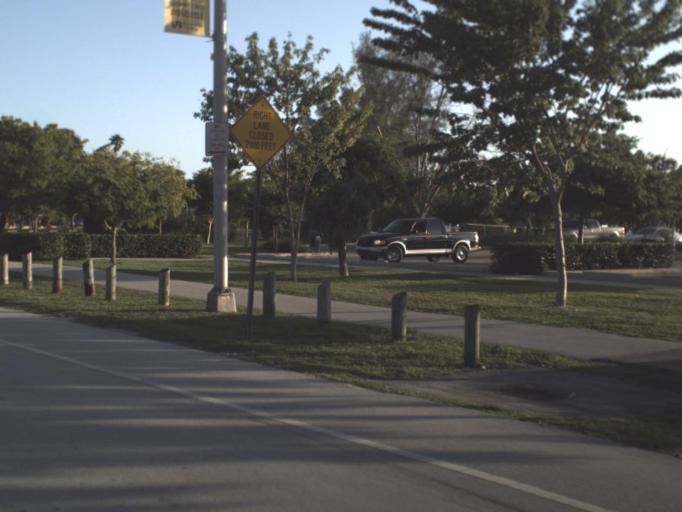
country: US
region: Florida
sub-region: Miami-Dade County
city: Key Biscayne
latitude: 25.7373
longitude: -80.1666
